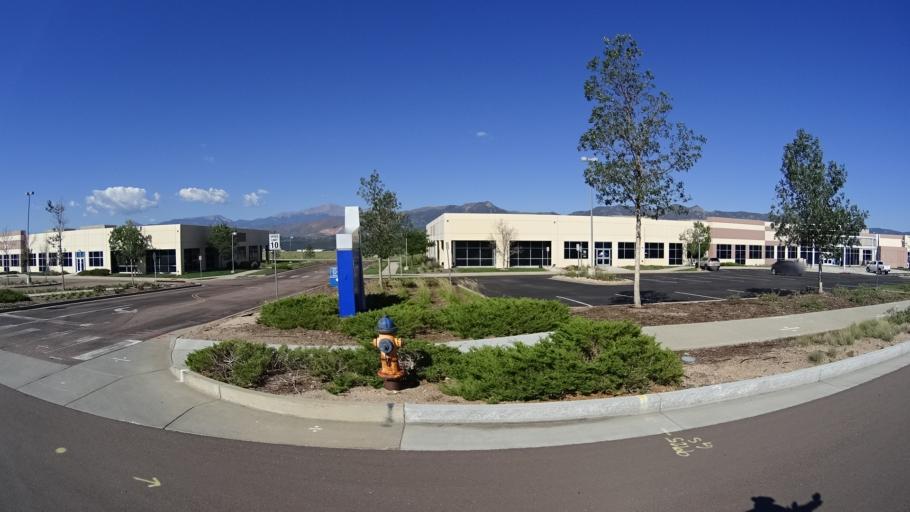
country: US
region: Colorado
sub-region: El Paso County
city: Air Force Academy
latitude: 38.9843
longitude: -104.8055
